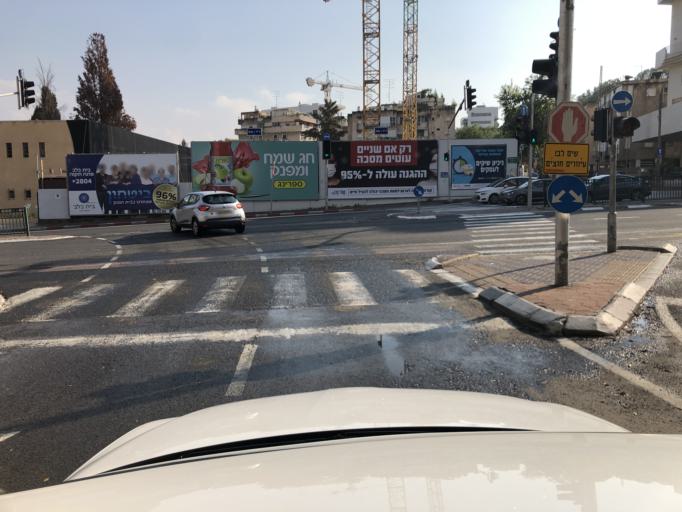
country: IL
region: Tel Aviv
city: Ramat Gan
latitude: 32.0901
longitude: 34.8191
